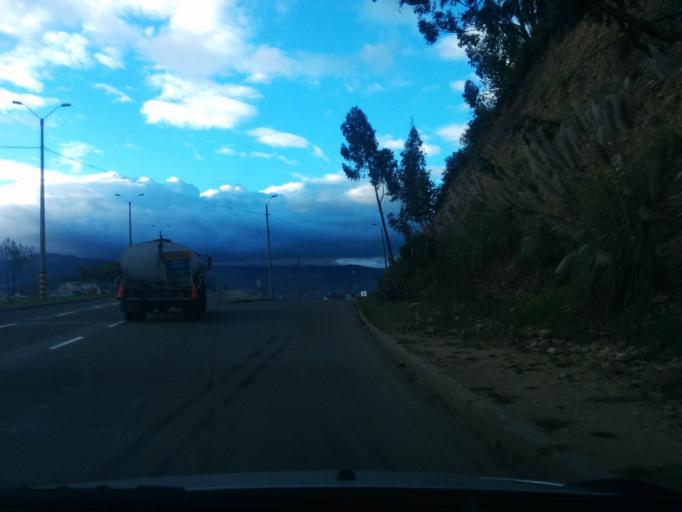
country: EC
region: Azuay
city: Cuenca
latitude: -2.8835
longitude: -78.9730
